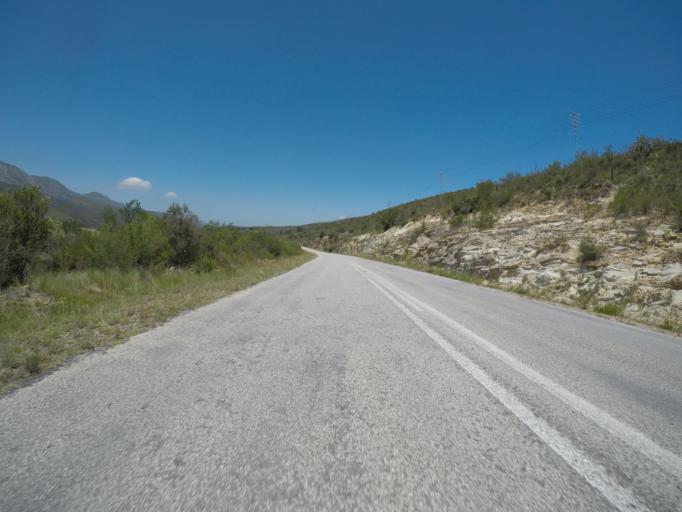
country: ZA
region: Eastern Cape
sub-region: Cacadu District Municipality
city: Kareedouw
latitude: -33.9116
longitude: 24.1675
